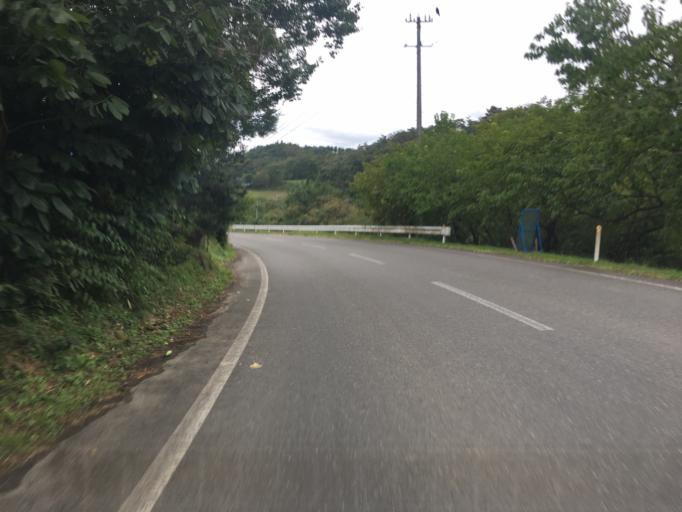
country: JP
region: Miyagi
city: Marumori
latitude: 37.8781
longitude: 140.7085
